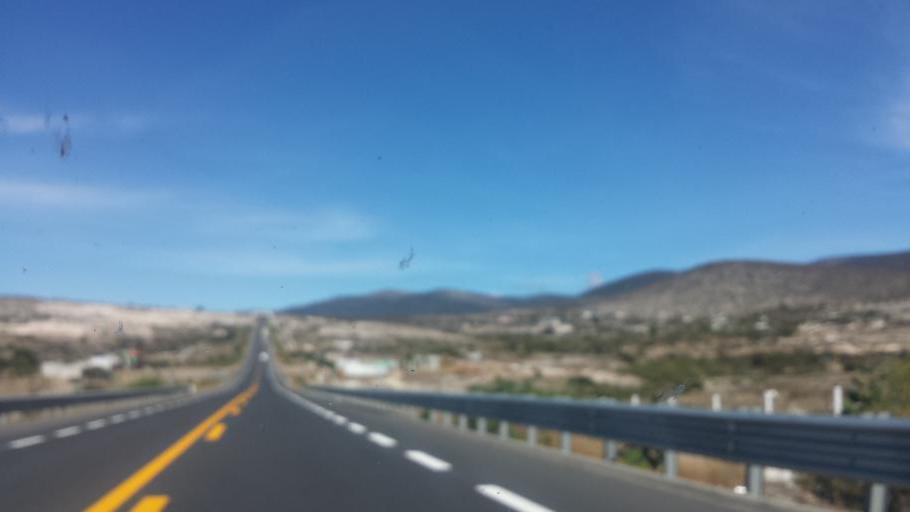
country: MX
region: Oaxaca
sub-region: Villa Tejupam de la Union
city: Villa Tejupam de la Union
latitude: 17.9261
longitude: -97.3585
